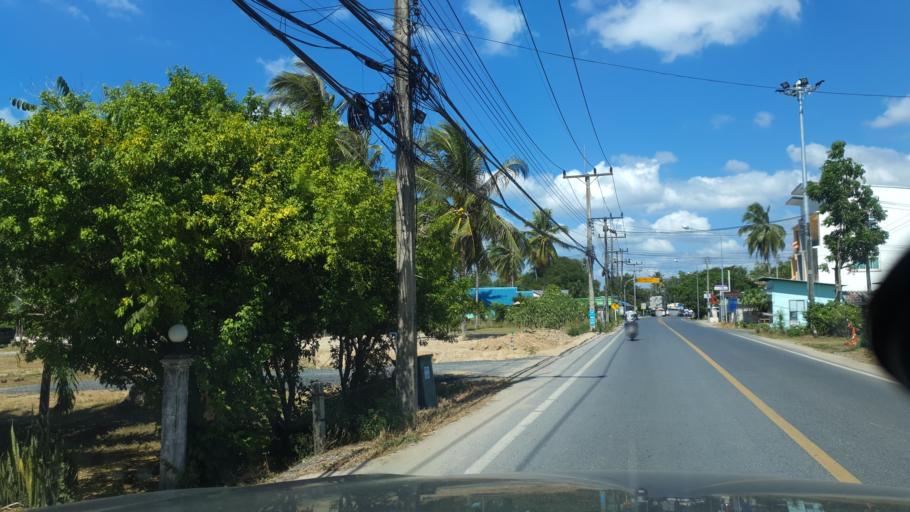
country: TH
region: Phuket
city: Thalang
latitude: 8.1274
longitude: 98.3080
